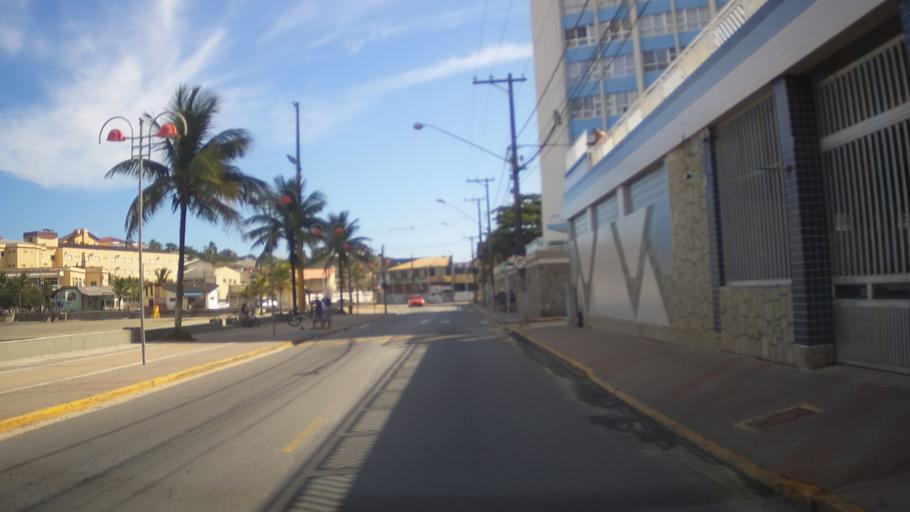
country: BR
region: Sao Paulo
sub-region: Itanhaem
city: Itanhaem
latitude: -24.1946
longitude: -46.8010
